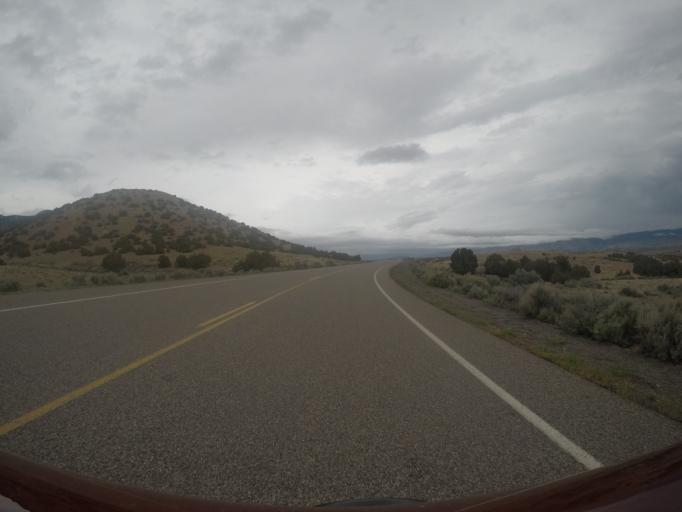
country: US
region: Wyoming
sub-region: Big Horn County
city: Lovell
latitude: 45.0659
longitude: -108.2563
